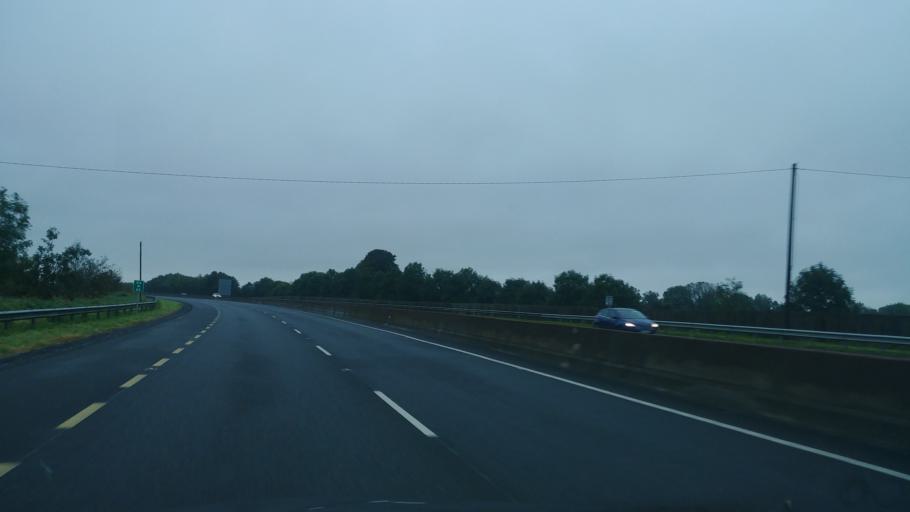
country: IE
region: Leinster
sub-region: An Iarmhi
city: An Muileann gCearr
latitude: 53.5087
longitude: -7.2485
